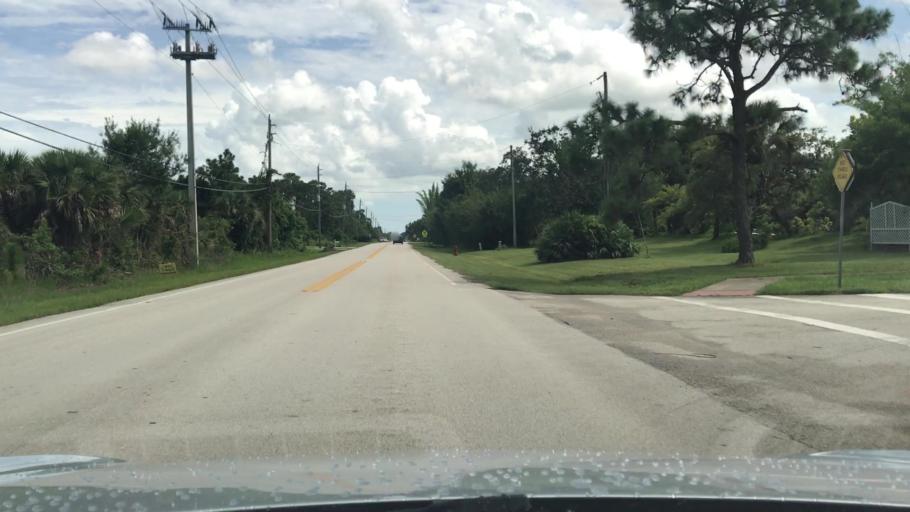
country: US
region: Florida
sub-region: Indian River County
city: Sebastian
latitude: 27.8013
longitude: -80.5020
